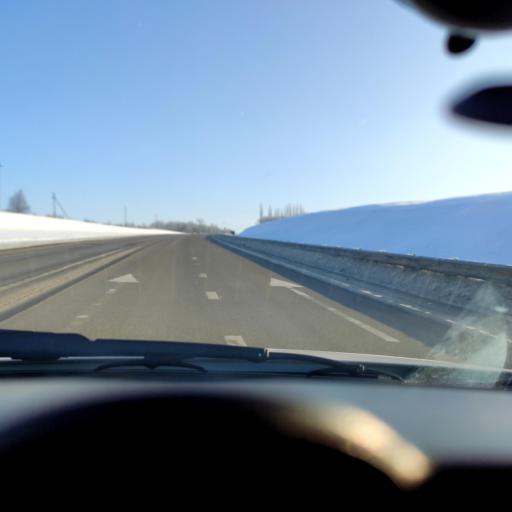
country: RU
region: Kursk
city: Tim
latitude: 51.6555
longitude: 36.9071
